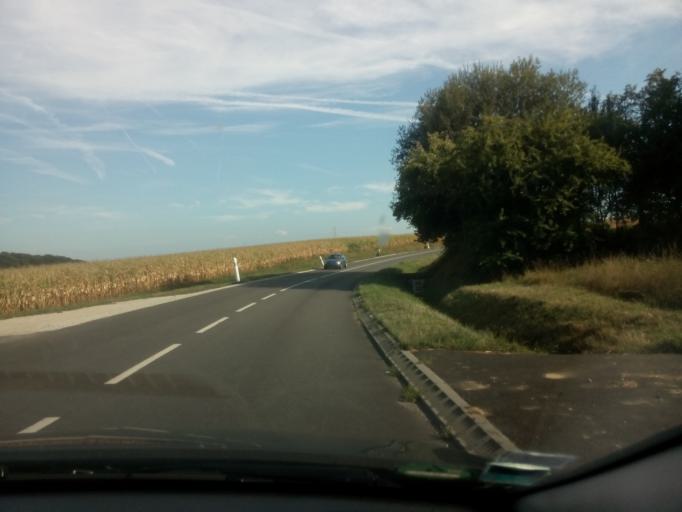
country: DE
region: Rheinland-Pfalz
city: Schweighofen
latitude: 49.0082
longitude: 7.9722
